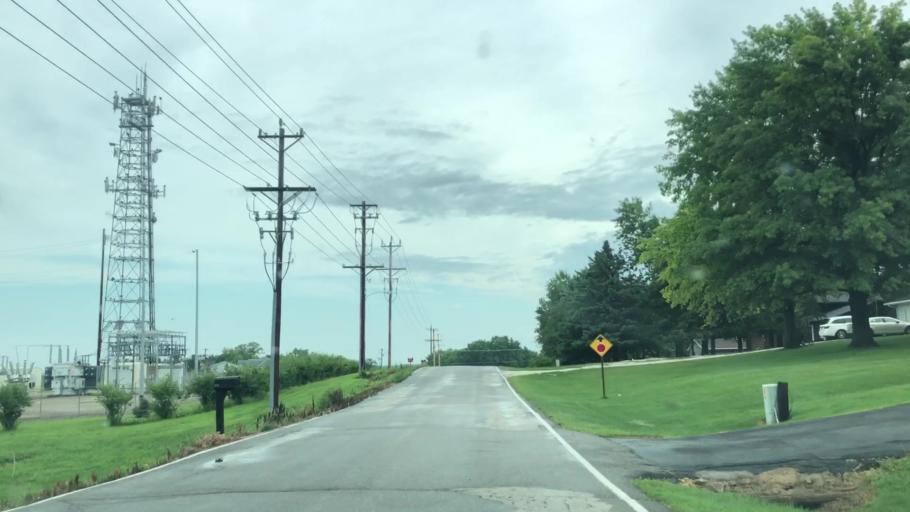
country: US
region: Iowa
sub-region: Marshall County
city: Marshalltown
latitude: 42.0471
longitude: -92.9612
